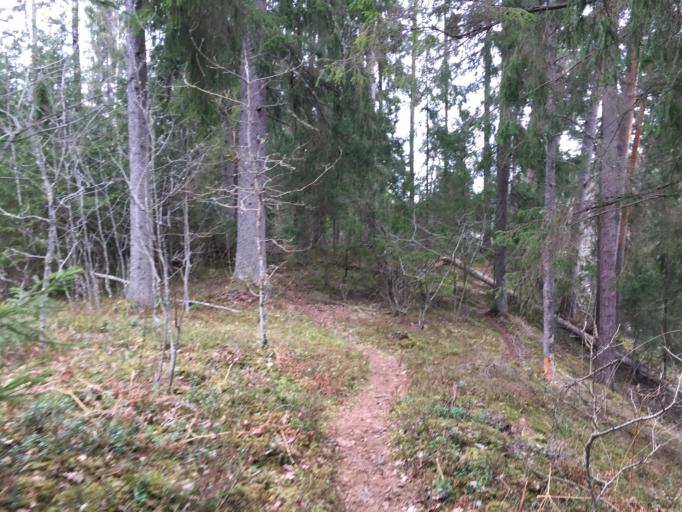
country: LV
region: Priekuli
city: Priekuli
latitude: 57.3287
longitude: 25.3931
